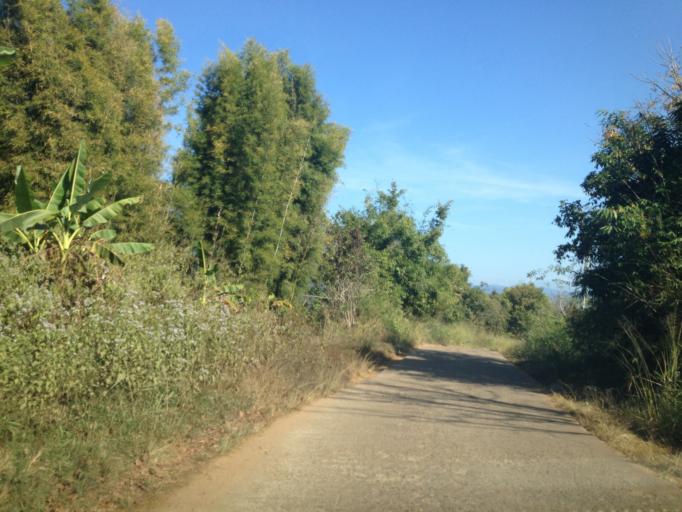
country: TH
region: Mae Hong Son
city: Ban Huai I Huak
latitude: 18.0483
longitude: 98.1667
